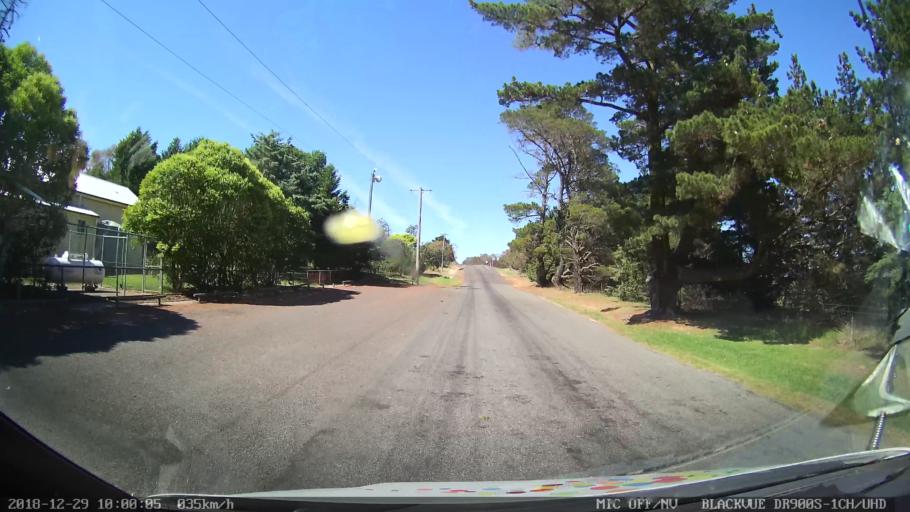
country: AU
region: New South Wales
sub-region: Goulburn Mulwaree
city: Goulburn
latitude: -34.7900
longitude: 149.4872
